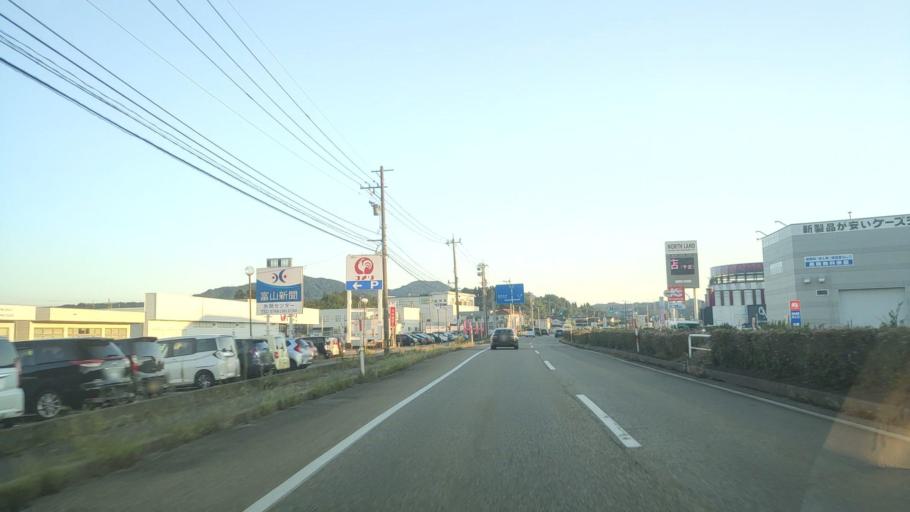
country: JP
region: Toyama
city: Himi
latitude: 36.8252
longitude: 136.9944
